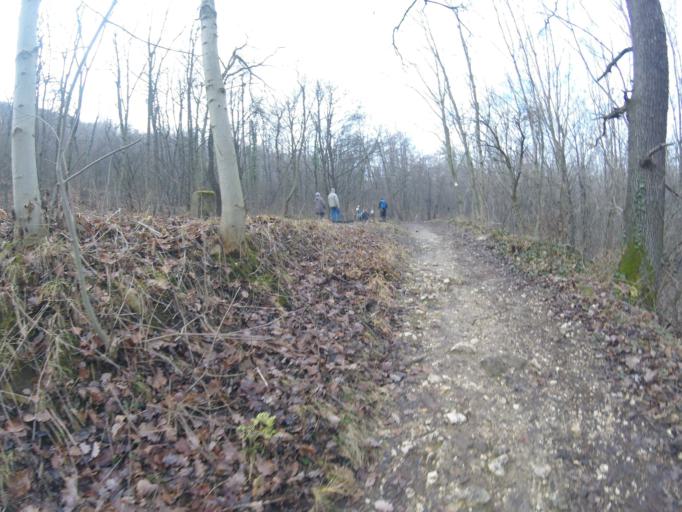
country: HU
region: Pest
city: Budakeszi
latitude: 47.5220
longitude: 18.9604
